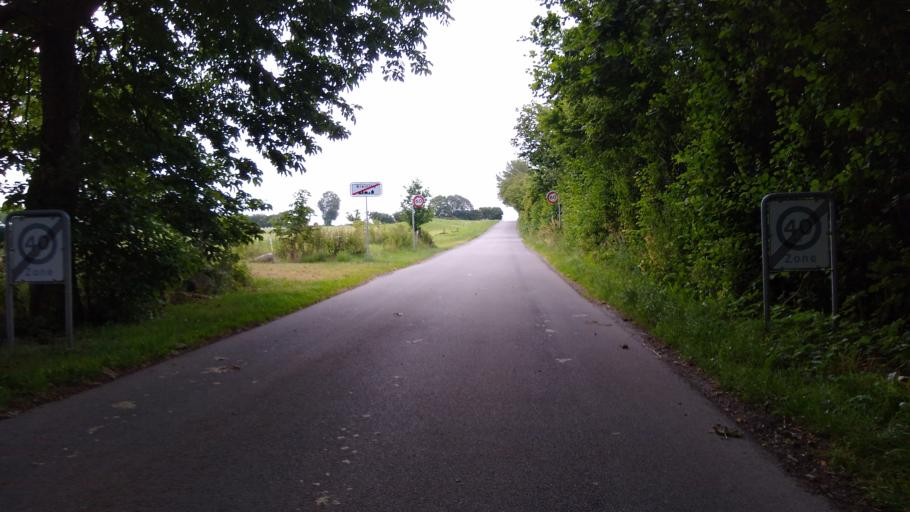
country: DK
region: South Denmark
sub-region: Vejle Kommune
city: Brejning
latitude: 55.6597
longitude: 9.6796
